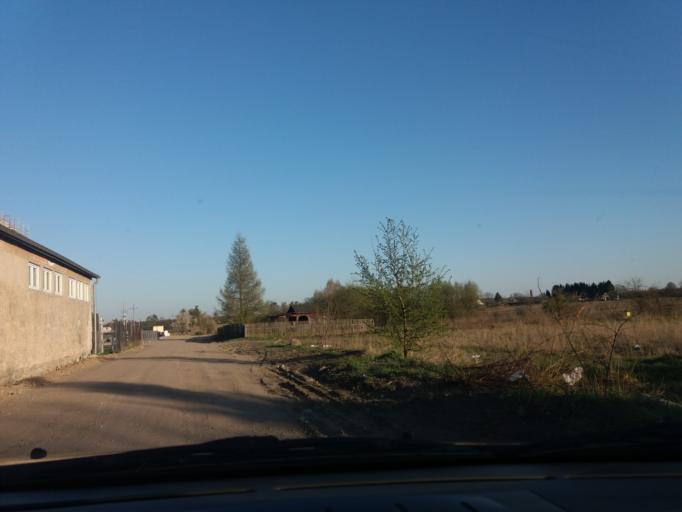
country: PL
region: Warmian-Masurian Voivodeship
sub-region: Powiat szczycienski
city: Szczytno
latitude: 53.5532
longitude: 20.9825
